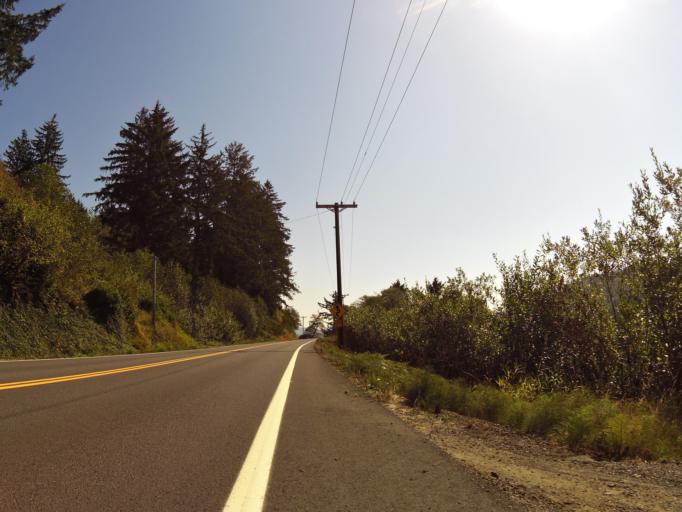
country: US
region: Oregon
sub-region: Tillamook County
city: Pacific City
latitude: 45.1832
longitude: -123.9453
